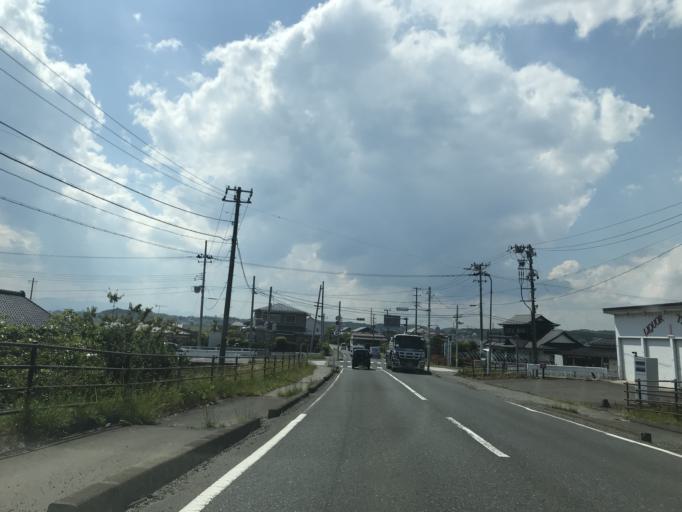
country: JP
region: Miyagi
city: Wakuya
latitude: 38.4732
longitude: 141.1238
